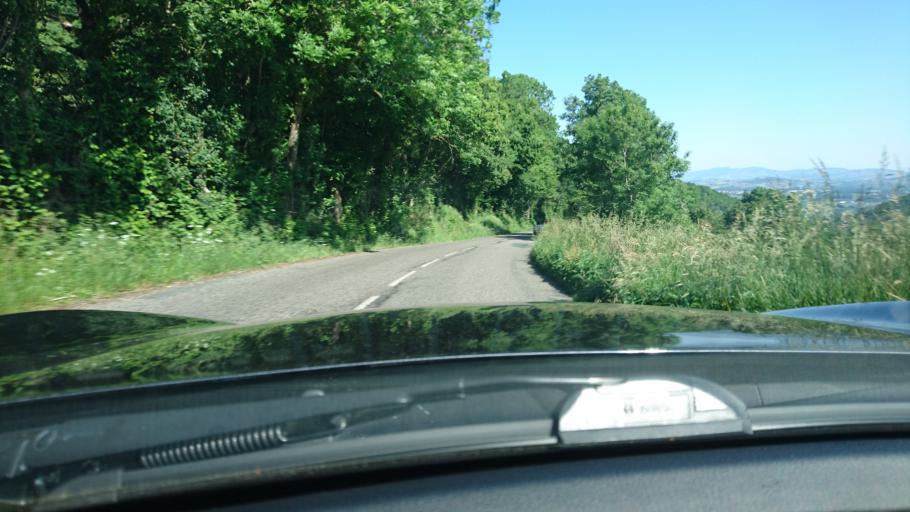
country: FR
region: Rhone-Alpes
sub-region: Departement du Rhone
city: Saint-Pierre-la-Palud
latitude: 45.7709
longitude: 4.5891
